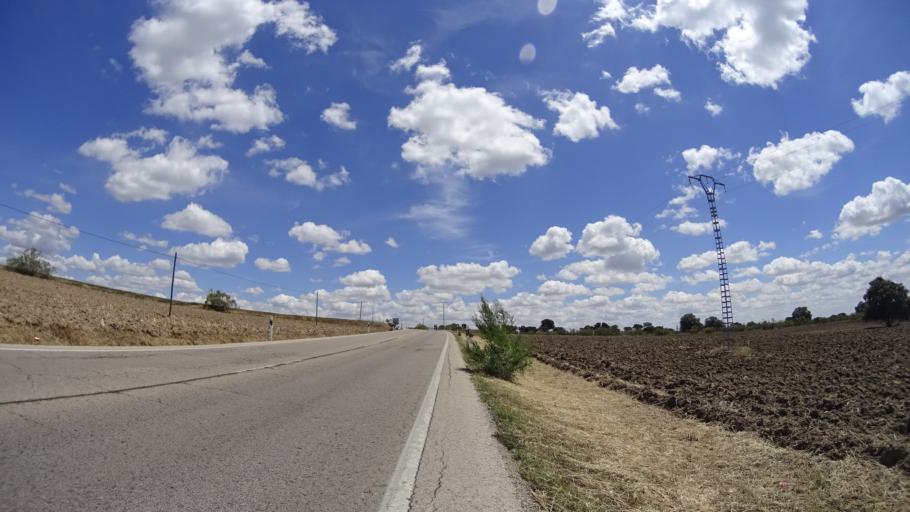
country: ES
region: Madrid
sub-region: Provincia de Madrid
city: Boadilla del Monte
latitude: 40.4133
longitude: -3.9335
